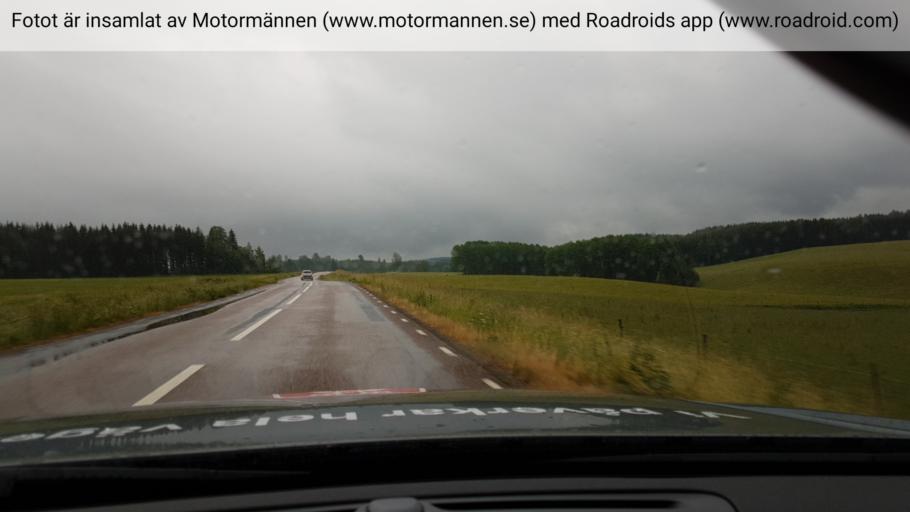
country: SE
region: Dalarna
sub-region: Avesta Kommun
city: Avesta
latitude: 59.9974
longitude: 16.0904
